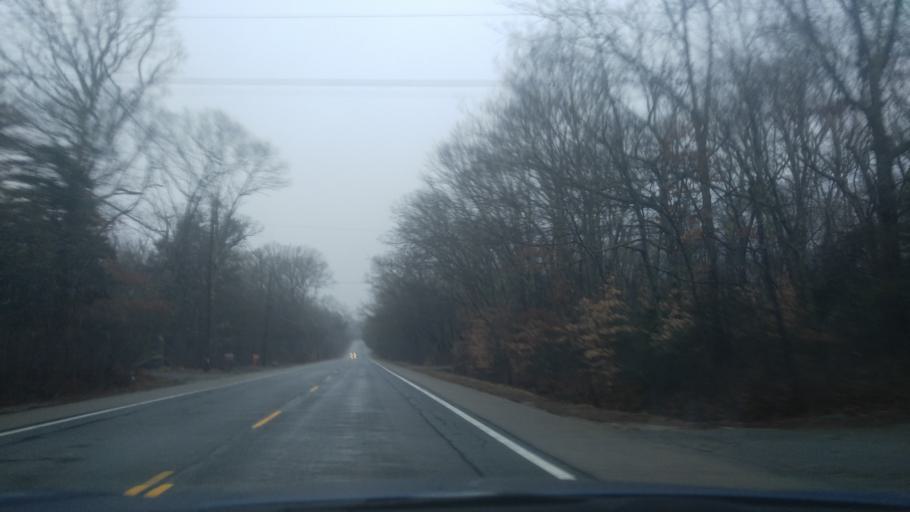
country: US
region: Rhode Island
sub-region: Washington County
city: Kingston
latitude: 41.4848
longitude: -71.5858
